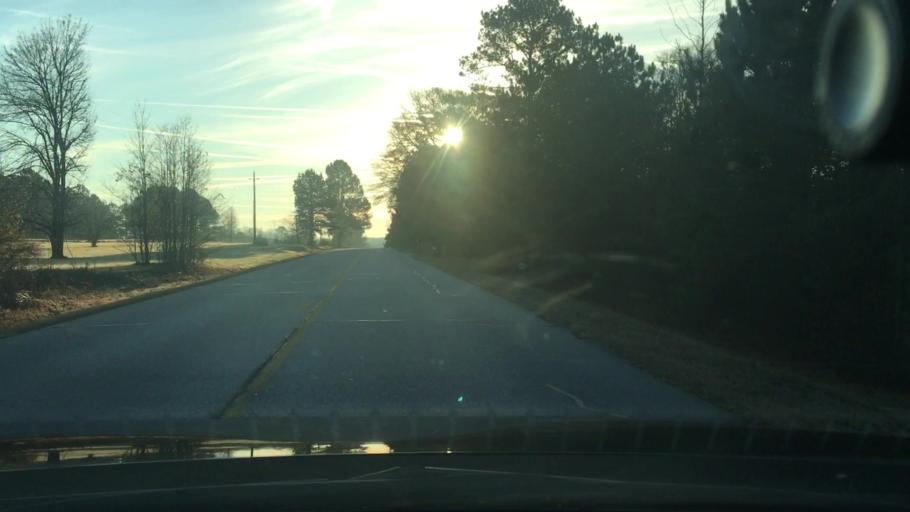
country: US
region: Georgia
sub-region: Coweta County
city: Senoia
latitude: 33.3234
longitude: -84.4912
